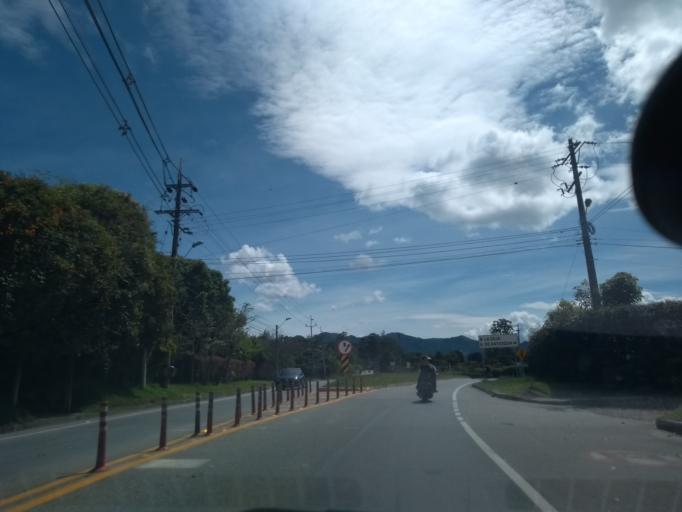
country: CO
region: Antioquia
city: Rionegro
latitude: 6.1067
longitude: -75.3864
